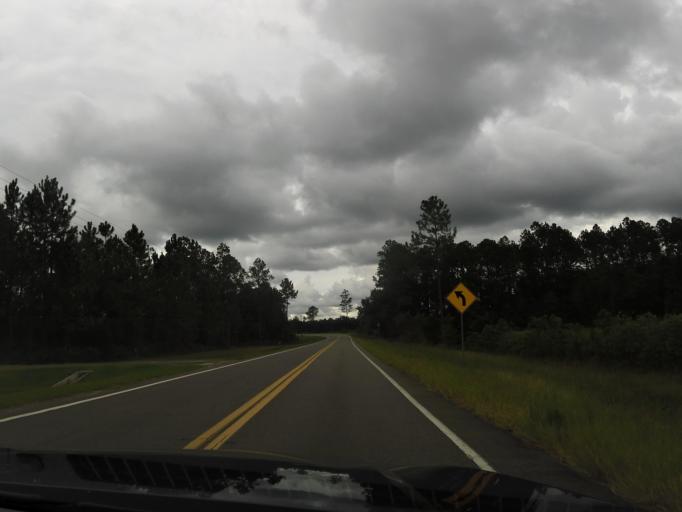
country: US
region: Florida
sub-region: Baker County
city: Macclenny
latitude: 30.4693
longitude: -82.1988
